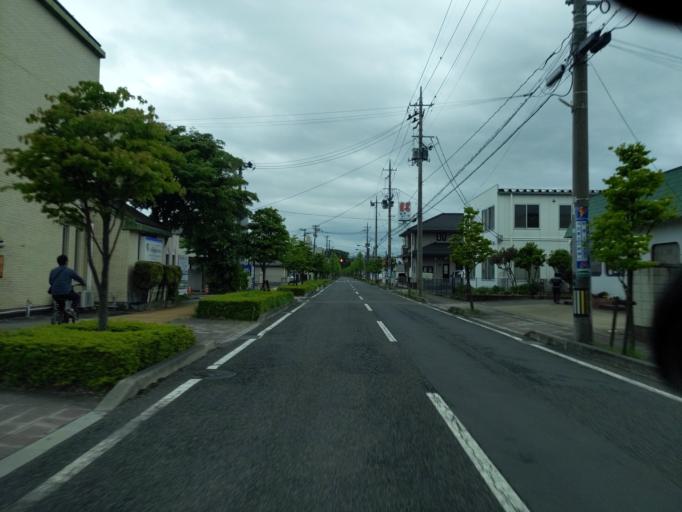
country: JP
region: Fukushima
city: Koriyama
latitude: 37.3571
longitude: 140.3623
